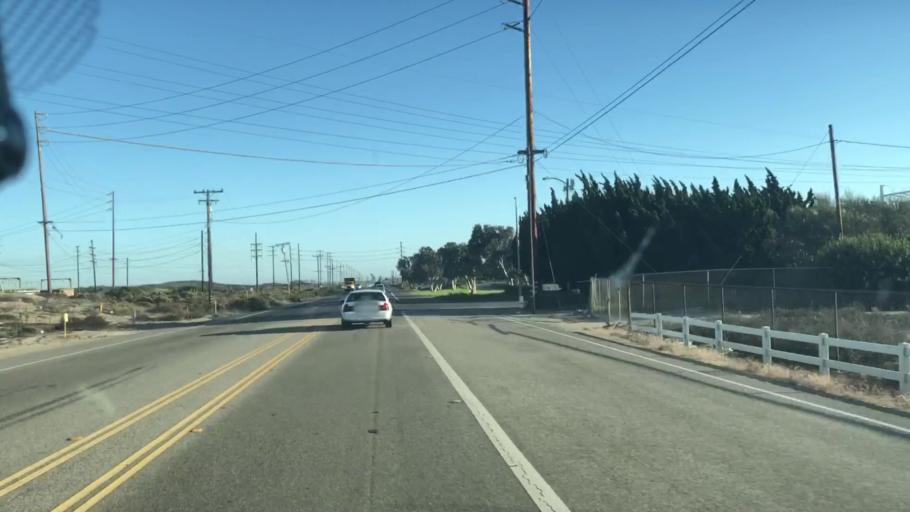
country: US
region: California
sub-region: Ventura County
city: Oxnard Shores
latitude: 34.2090
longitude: -119.2487
